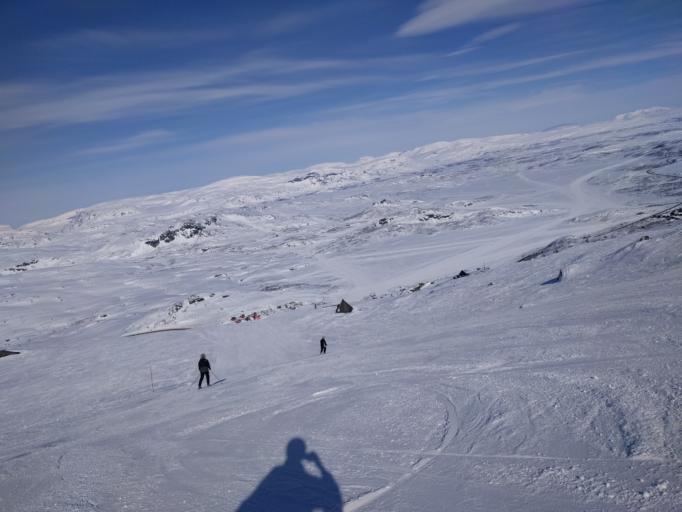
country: NO
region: Troms
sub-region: Lavangen
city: Tennevoll
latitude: 68.4199
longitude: 18.1021
